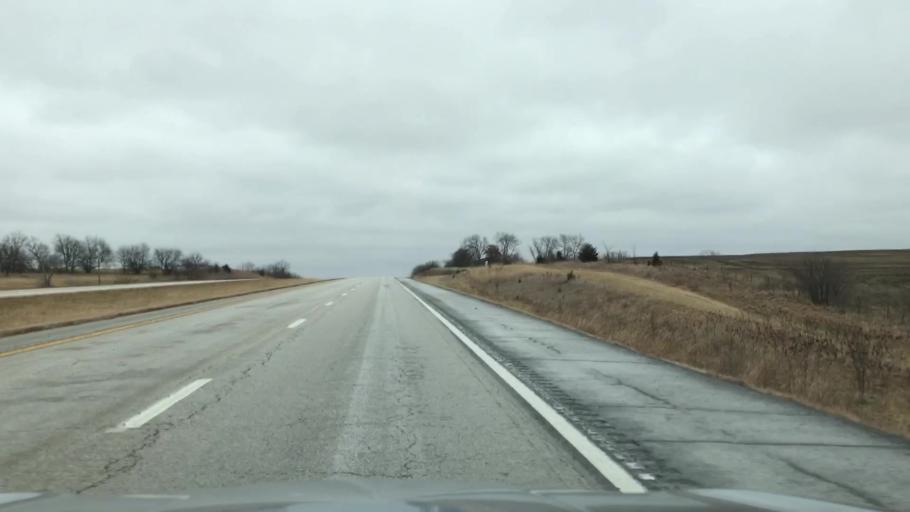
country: US
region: Missouri
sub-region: Caldwell County
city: Hamilton
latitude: 39.7501
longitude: -94.1100
